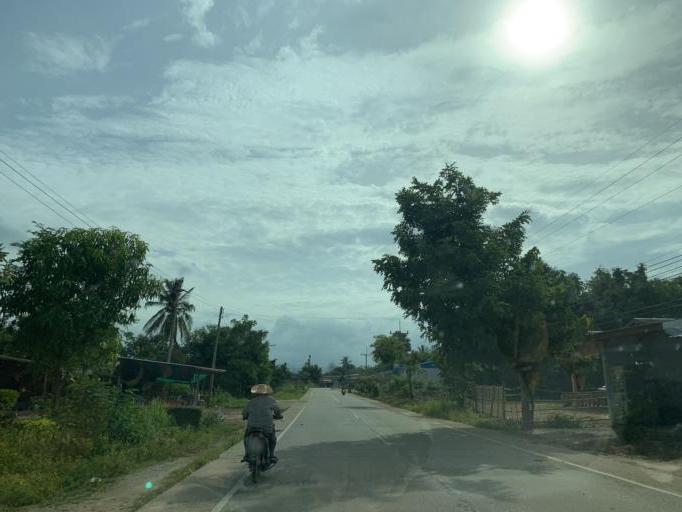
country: TH
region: Nakhon Sawan
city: Mae Wong
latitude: 15.8419
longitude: 99.4196
